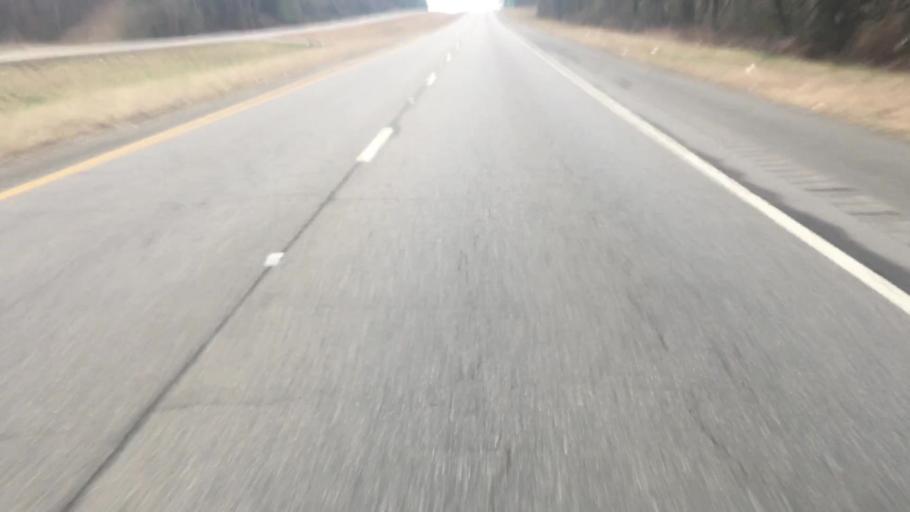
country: US
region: Alabama
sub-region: Walker County
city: Sumiton
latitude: 33.7694
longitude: -87.0718
